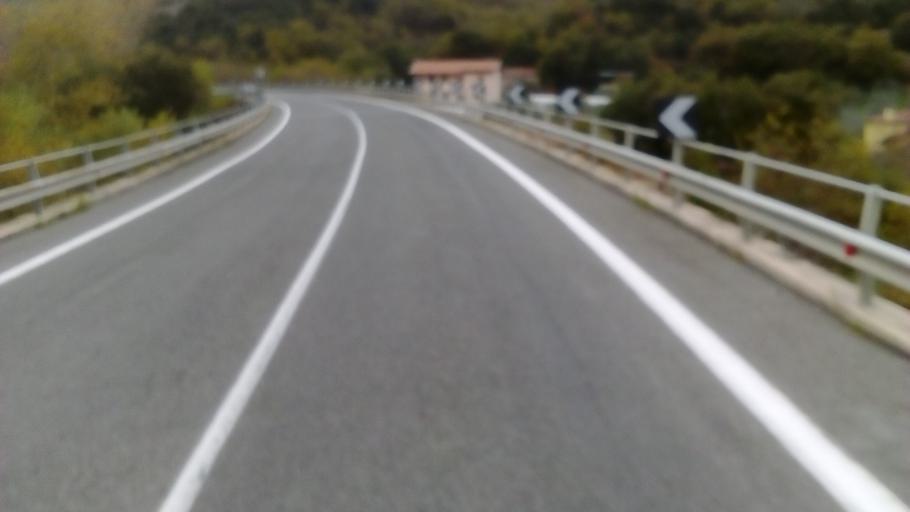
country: IT
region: Molise
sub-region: Provincia di Campobasso
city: Trivento
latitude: 41.7979
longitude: 14.5548
